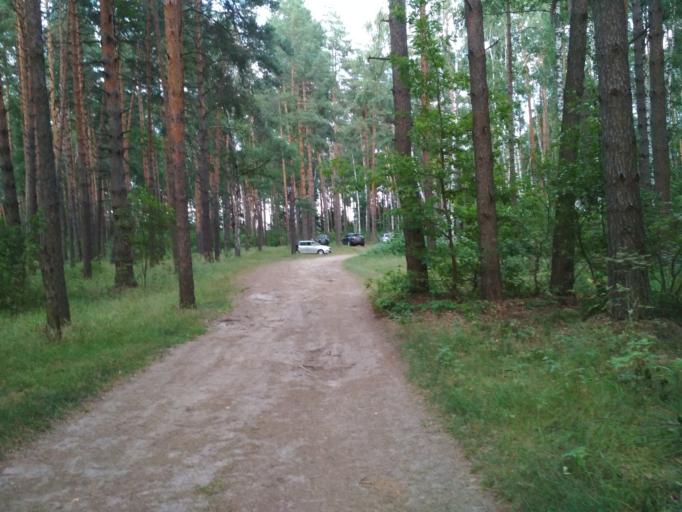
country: RU
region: Rjazan
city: Solotcha
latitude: 54.8299
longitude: 39.9477
